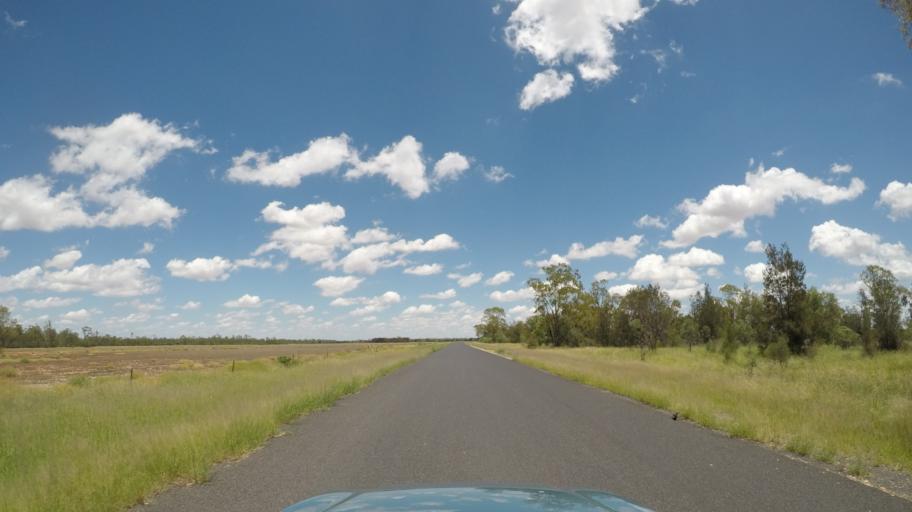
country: AU
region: Queensland
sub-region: Goondiwindi
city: Goondiwindi
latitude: -28.1692
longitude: 150.4670
